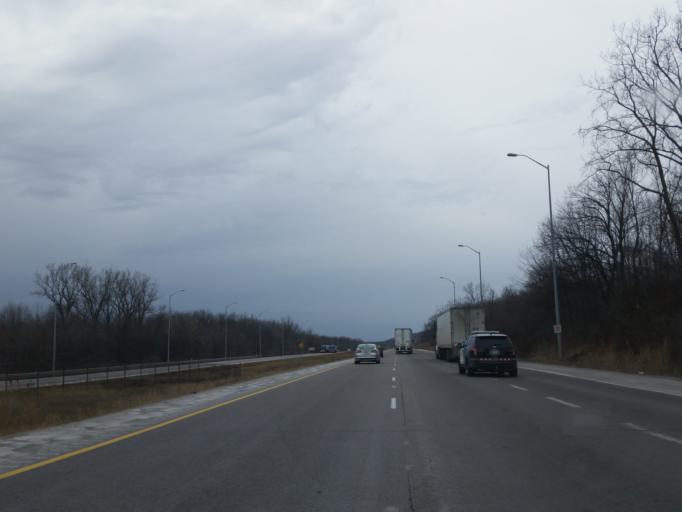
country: CA
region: Ontario
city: Quinte West
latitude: 44.1085
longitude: -77.6641
